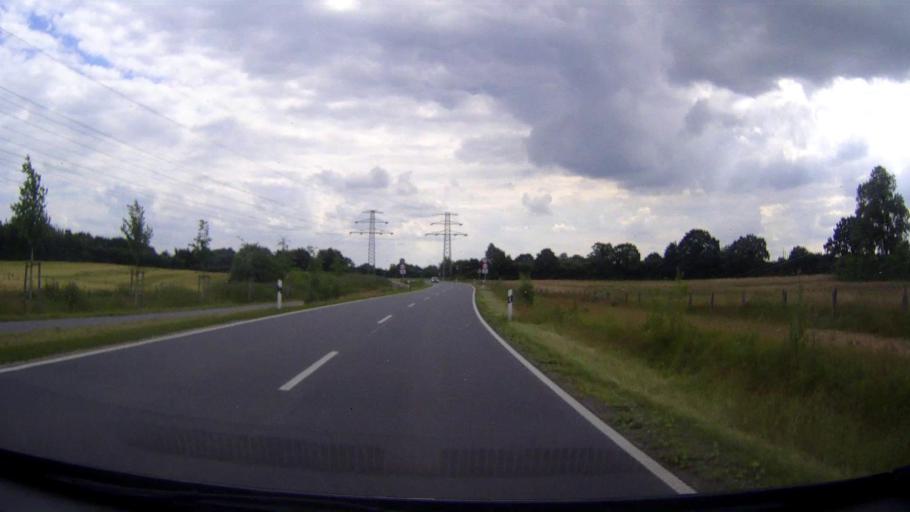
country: DE
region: Schleswig-Holstein
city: Badendorf
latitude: 53.8821
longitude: 10.6038
